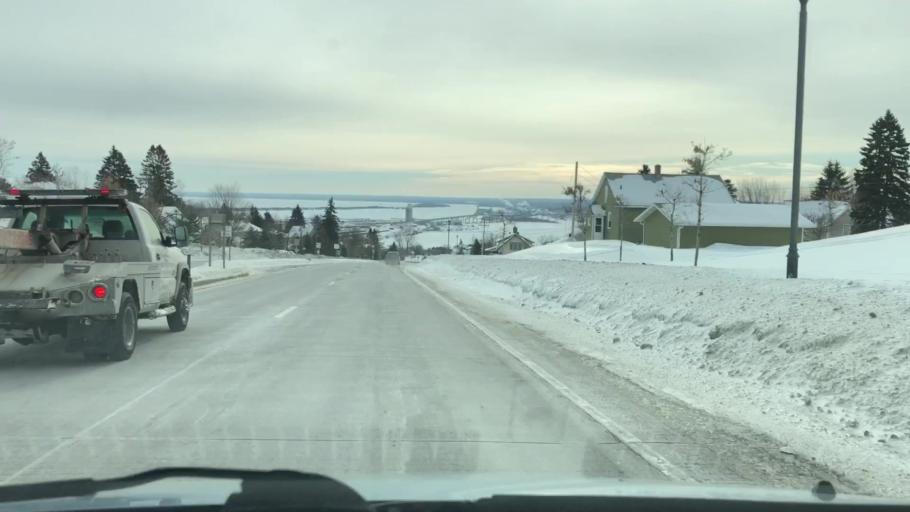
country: US
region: Minnesota
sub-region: Saint Louis County
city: Duluth
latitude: 46.7739
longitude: -92.1417
